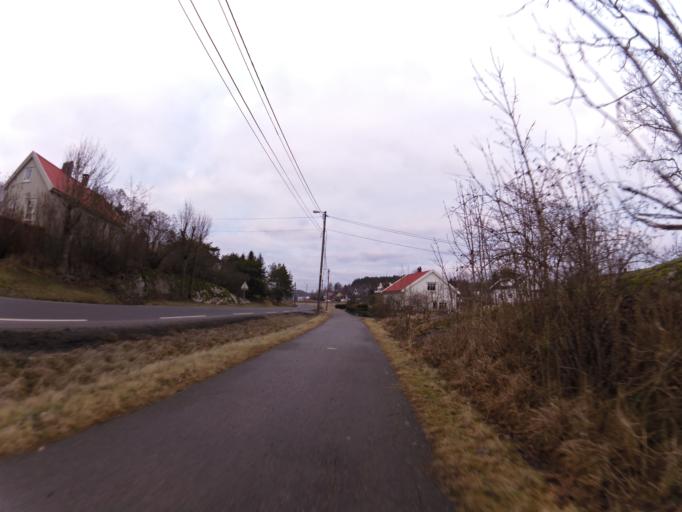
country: NO
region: Ostfold
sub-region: Fredrikstad
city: Fredrikstad
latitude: 59.1999
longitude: 10.8866
